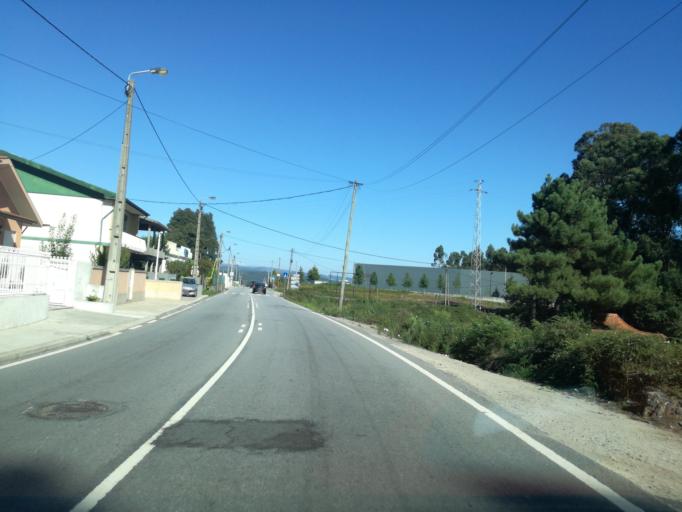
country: PT
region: Porto
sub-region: Trofa
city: Sao Romao do Coronado
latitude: 41.2827
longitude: -8.5849
